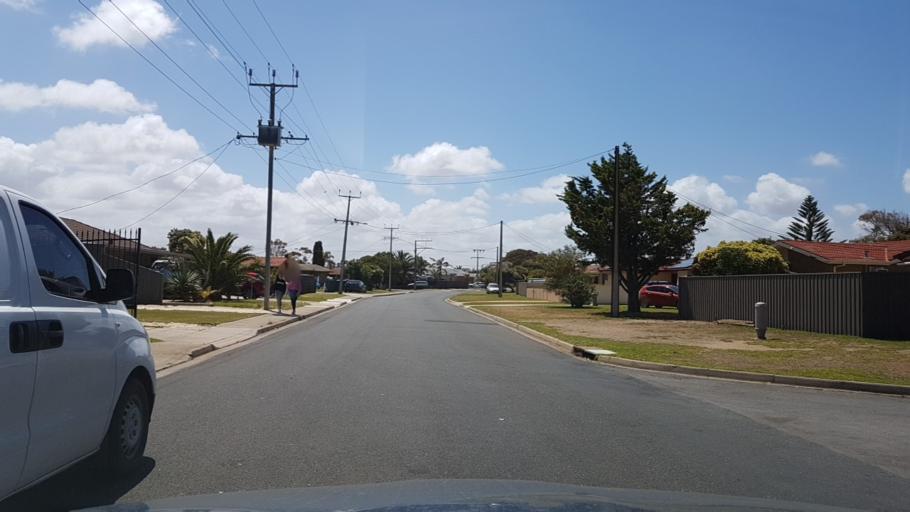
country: AU
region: South Australia
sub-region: Onkaparinga
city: Seaford
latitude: -35.1871
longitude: 138.4704
